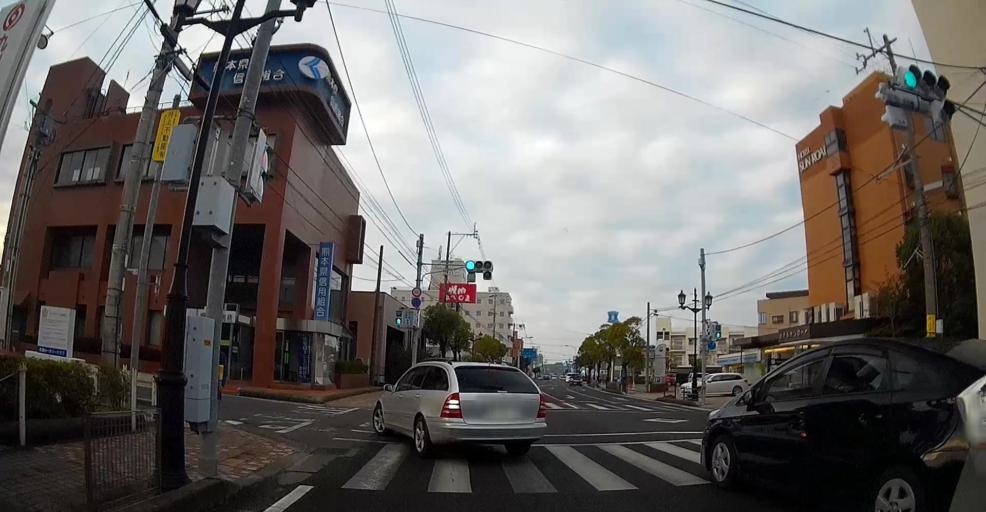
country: JP
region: Kumamoto
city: Hondo
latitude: 32.4541
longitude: 130.1944
